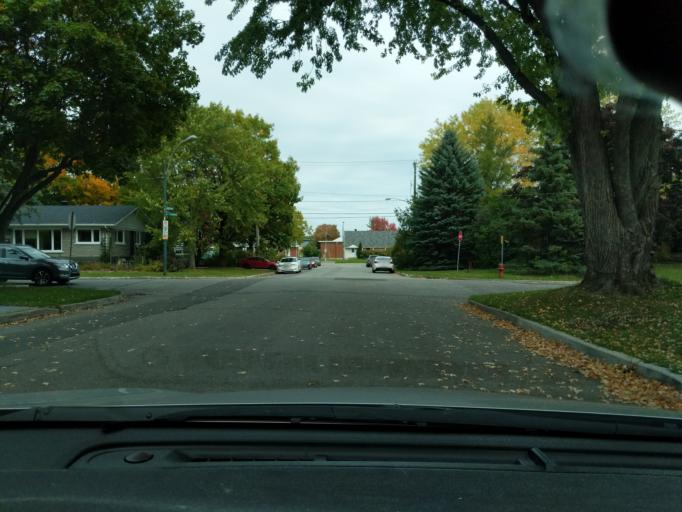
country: CA
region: Quebec
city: L'Ancienne-Lorette
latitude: 46.7710
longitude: -71.2902
